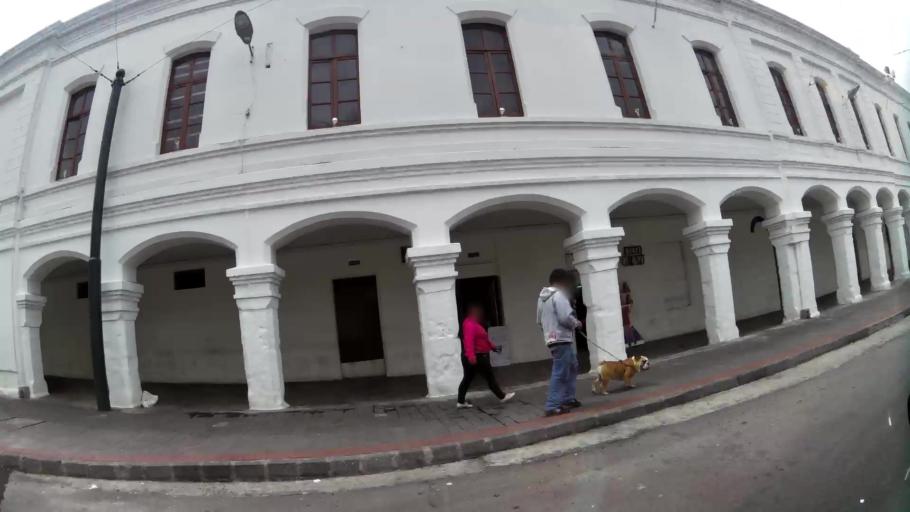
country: EC
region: Pichincha
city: Quito
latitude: -0.2234
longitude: -78.5124
